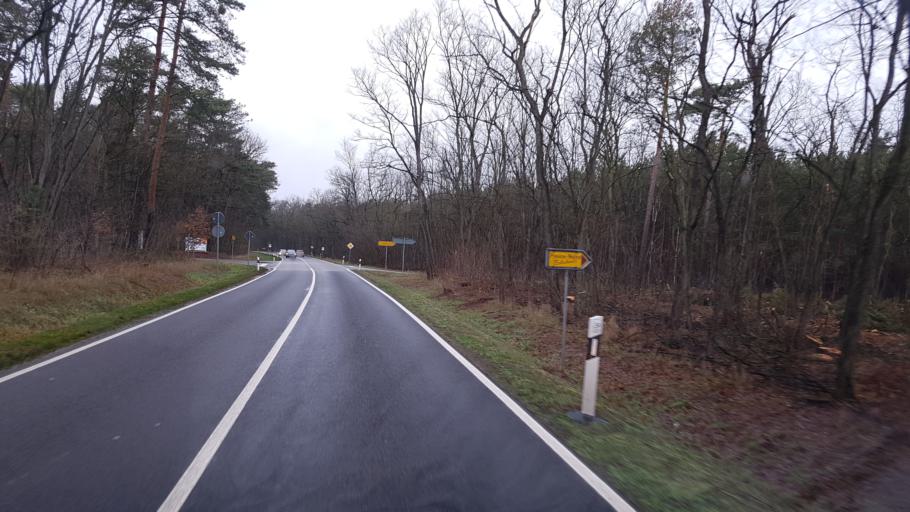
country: DE
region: Brandenburg
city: Calau
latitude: 51.7227
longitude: 14.0086
